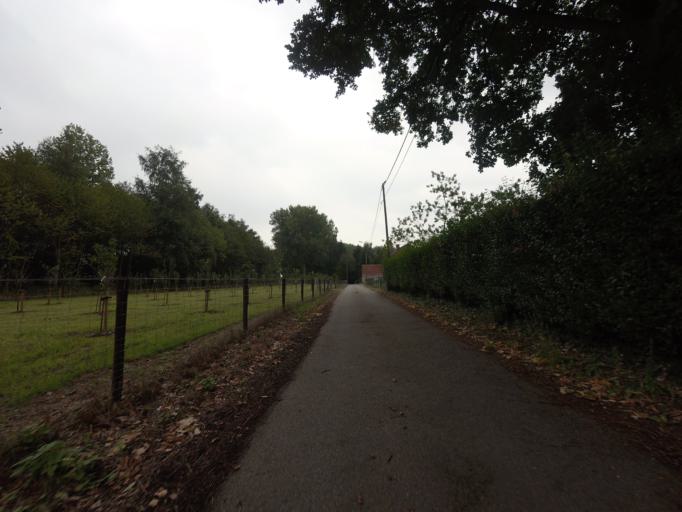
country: BE
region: Flanders
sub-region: Provincie Vlaams-Brabant
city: Boortmeerbeek
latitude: 50.9728
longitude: 4.5715
